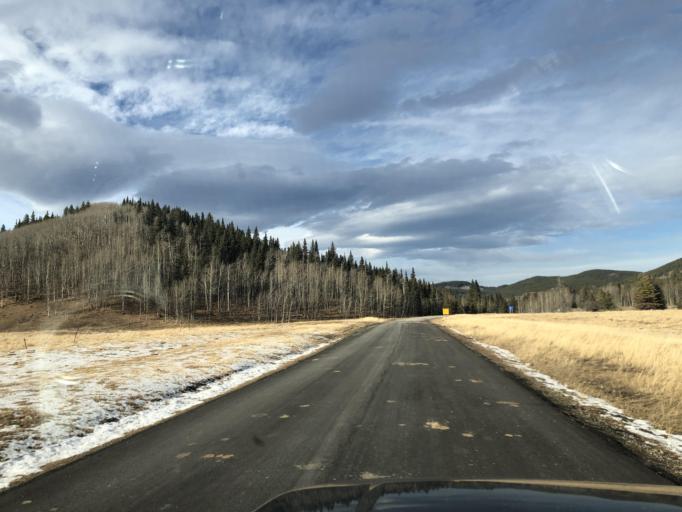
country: CA
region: Alberta
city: Cochrane
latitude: 51.0437
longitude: -114.8667
